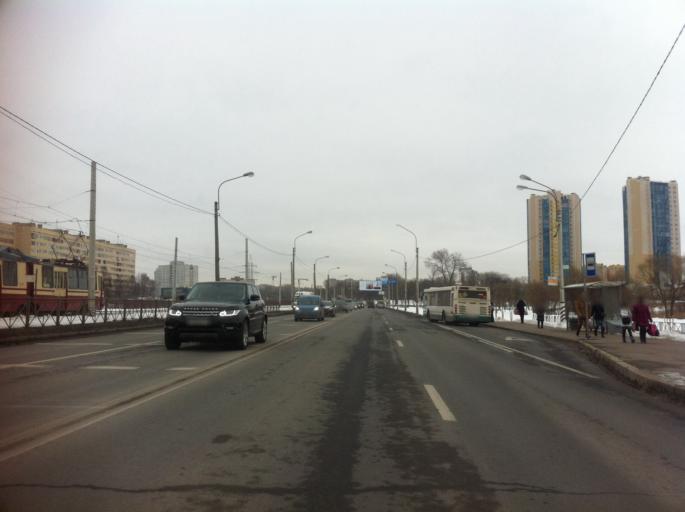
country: RU
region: St.-Petersburg
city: Uritsk
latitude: 59.8457
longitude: 30.2041
